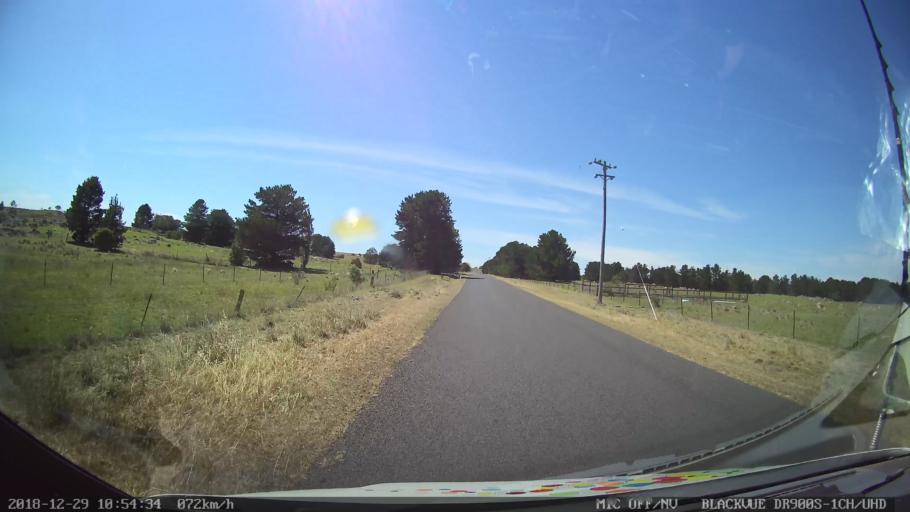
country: AU
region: New South Wales
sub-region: Palerang
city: Bungendore
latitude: -35.1158
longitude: 149.5278
